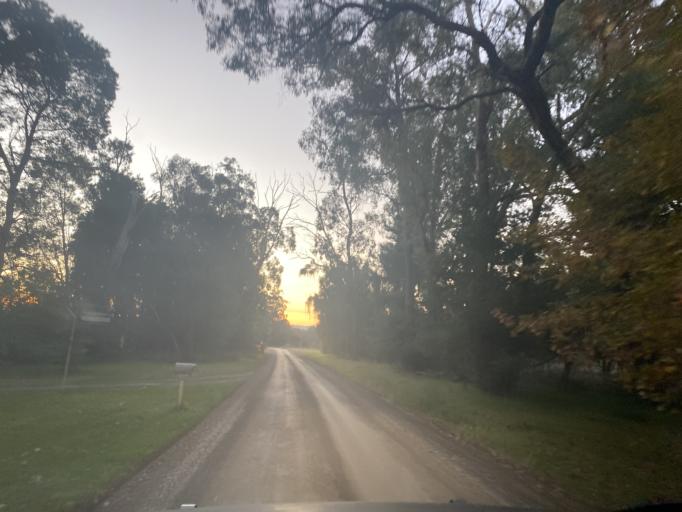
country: AU
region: Victoria
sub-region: Yarra Ranges
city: Healesville
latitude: -37.4205
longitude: 145.4689
